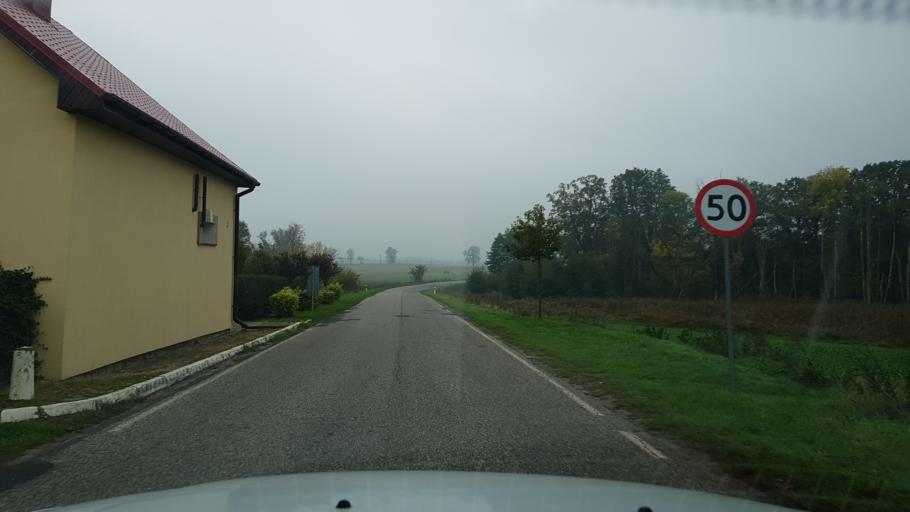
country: PL
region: West Pomeranian Voivodeship
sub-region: Powiat stargardzki
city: Dolice
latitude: 53.1574
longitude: 15.2384
